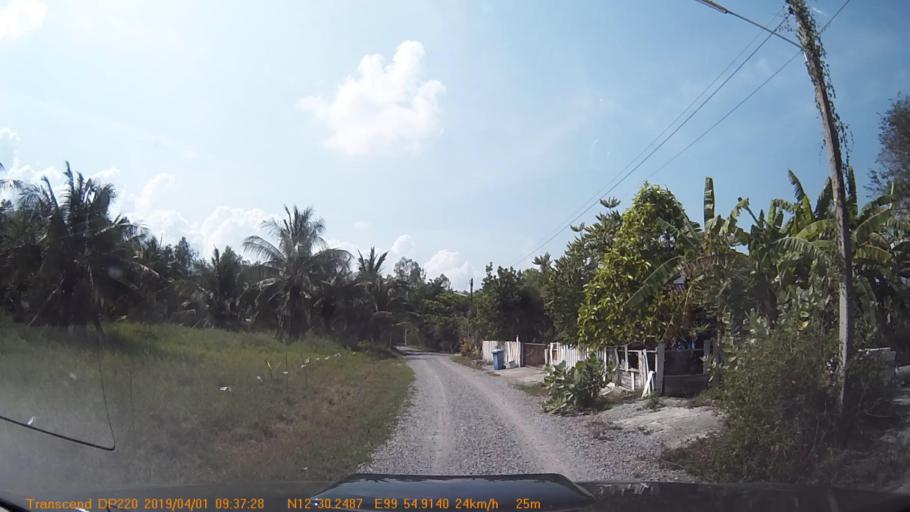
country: TH
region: Prachuap Khiri Khan
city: Hua Hin
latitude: 12.5040
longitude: 99.9153
